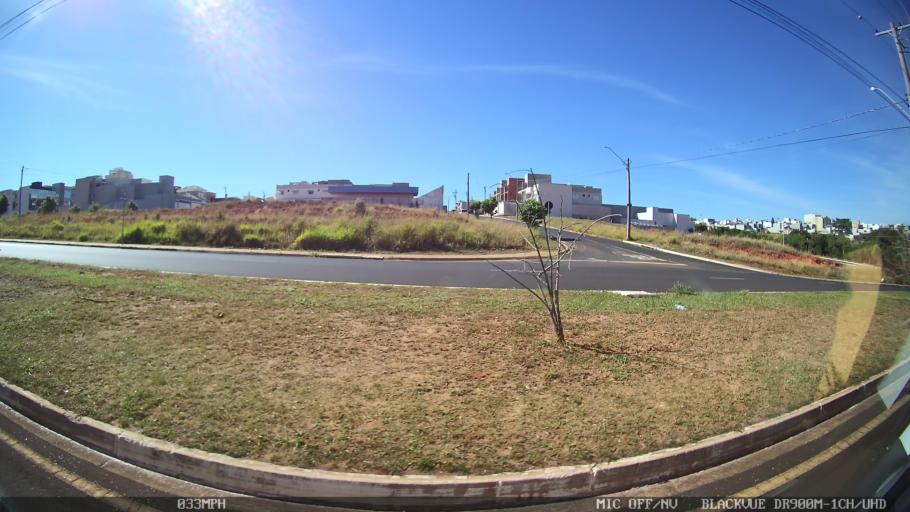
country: BR
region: Sao Paulo
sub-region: Franca
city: Franca
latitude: -20.5364
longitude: -47.3759
